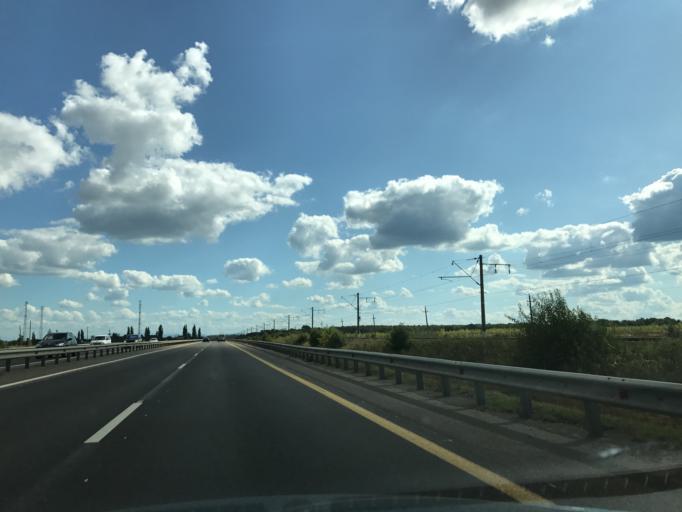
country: RU
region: Adygeya
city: Adygeysk
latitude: 44.8125
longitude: 39.2278
